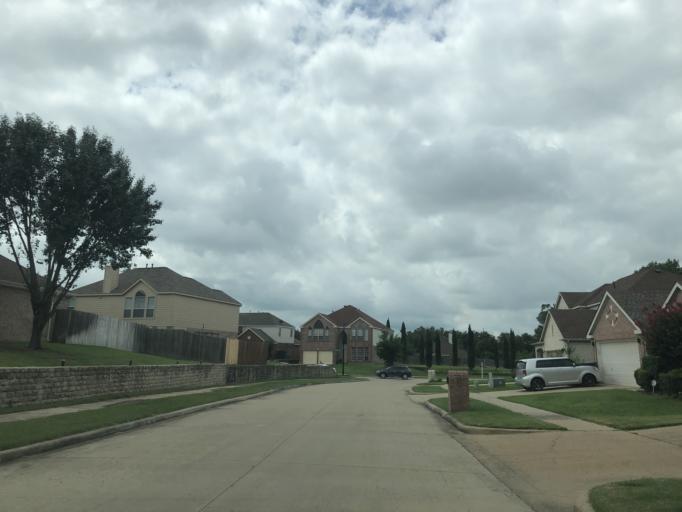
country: US
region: Texas
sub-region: Dallas County
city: Sunnyvale
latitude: 32.8412
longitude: -96.5717
